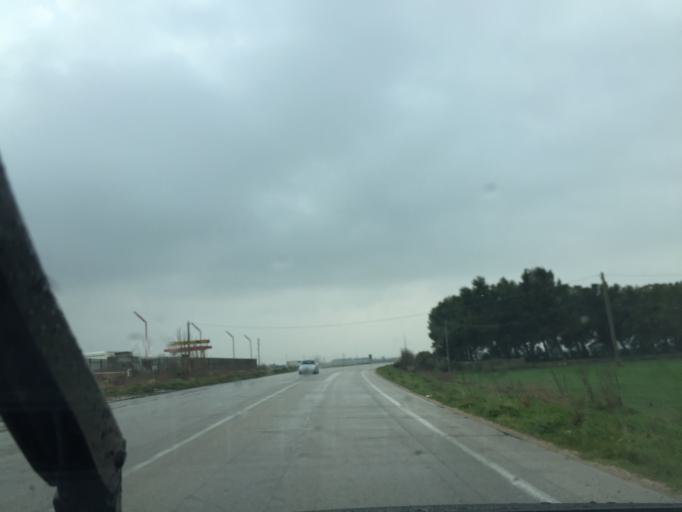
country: IT
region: Apulia
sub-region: Provincia di Foggia
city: Foggia
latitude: 41.4863
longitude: 15.5220
